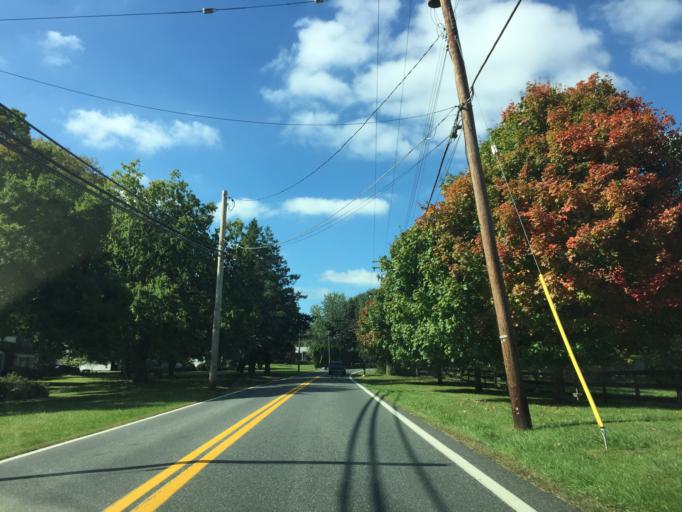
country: US
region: Maryland
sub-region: Baltimore County
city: Kingsville
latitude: 39.4697
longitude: -76.4445
